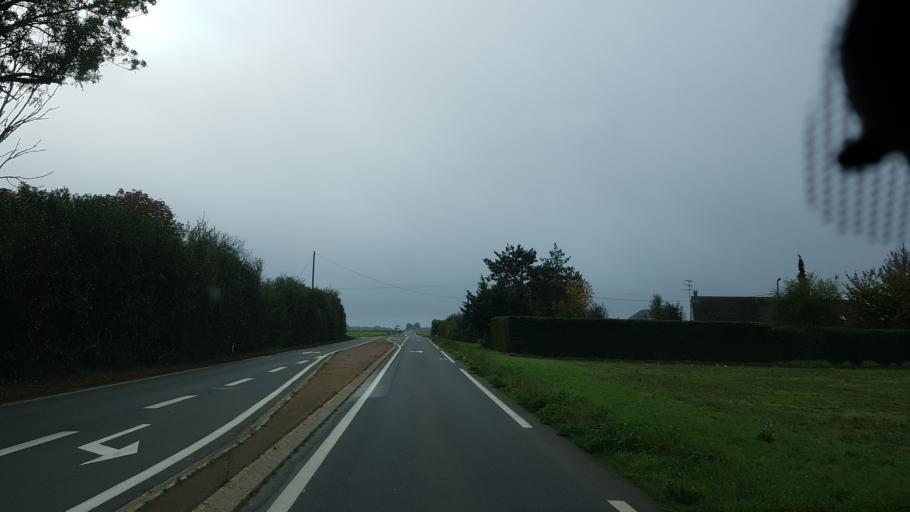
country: FR
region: Ile-de-France
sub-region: Departement de l'Essonne
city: Corbreuse
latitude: 48.4241
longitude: 1.9633
